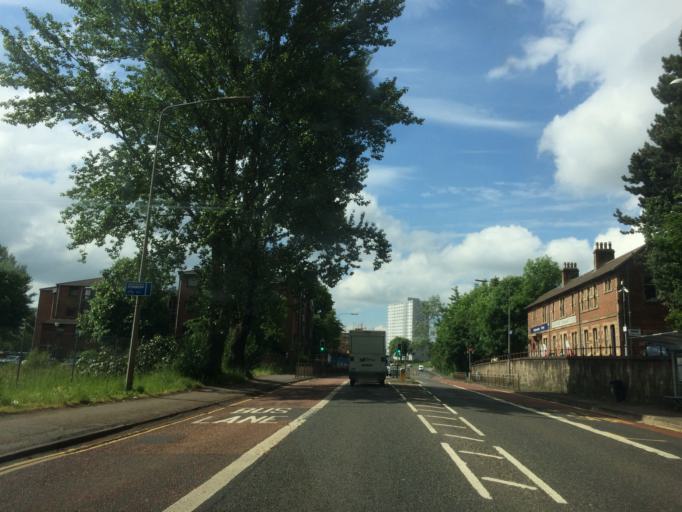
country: GB
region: Scotland
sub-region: East Renfrewshire
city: Giffnock
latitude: 55.8243
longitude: -4.3004
